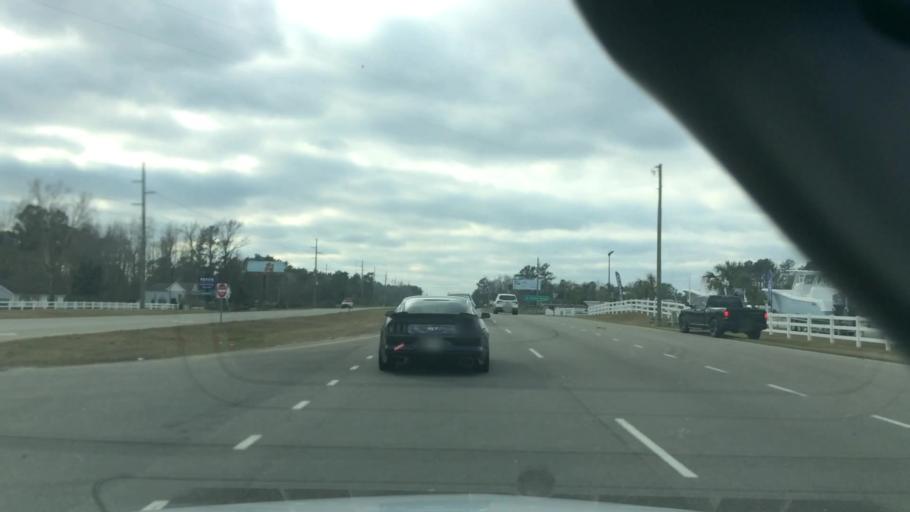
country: US
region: North Carolina
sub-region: Brunswick County
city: Shallotte
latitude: 34.0088
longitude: -78.2973
